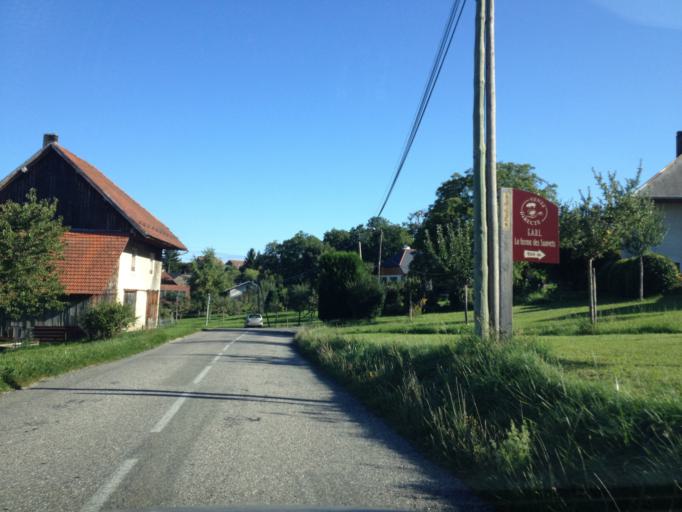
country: FR
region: Rhone-Alpes
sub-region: Departement de la Haute-Savoie
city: Cusy
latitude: 45.7288
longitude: 6.0063
